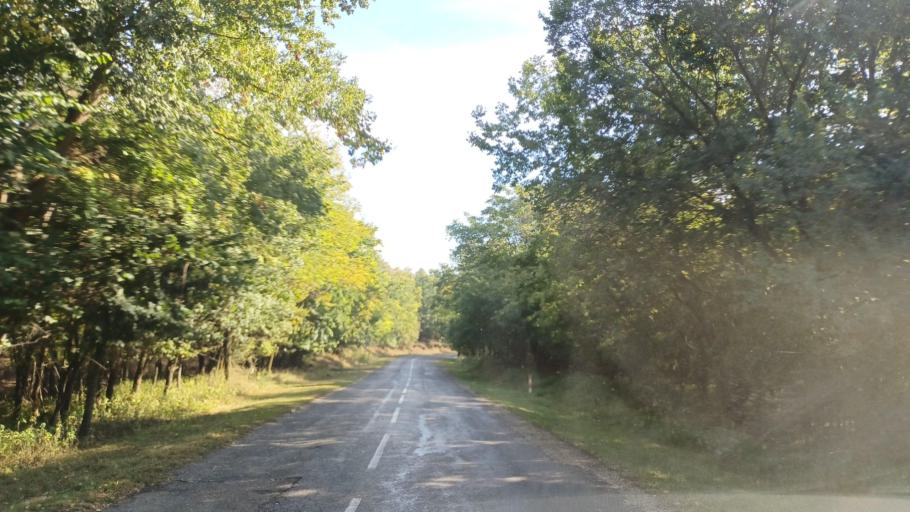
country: HU
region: Tolna
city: Pincehely
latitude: 46.6655
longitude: 18.4823
